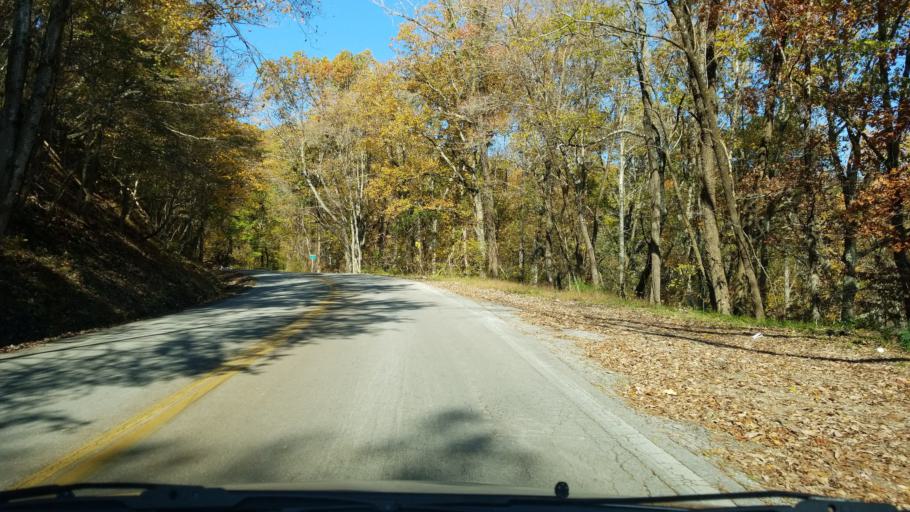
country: US
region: Tennessee
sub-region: Hamilton County
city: Soddy-Daisy
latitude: 35.2430
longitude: -85.1957
